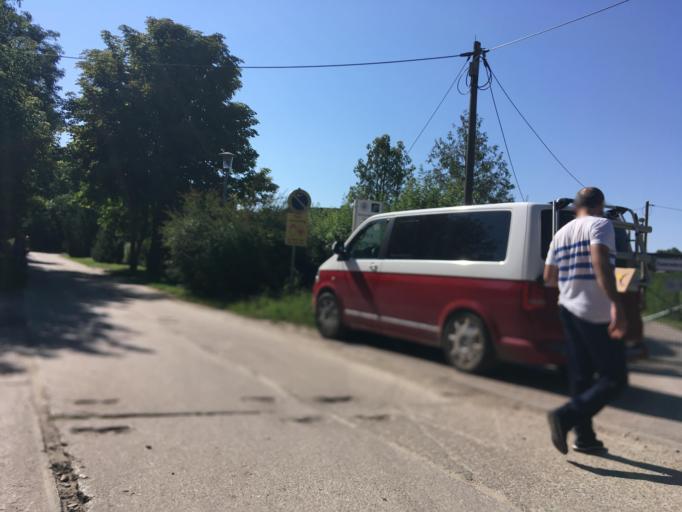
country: DE
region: Brandenburg
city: Gross Koris
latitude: 52.1865
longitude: 13.7102
